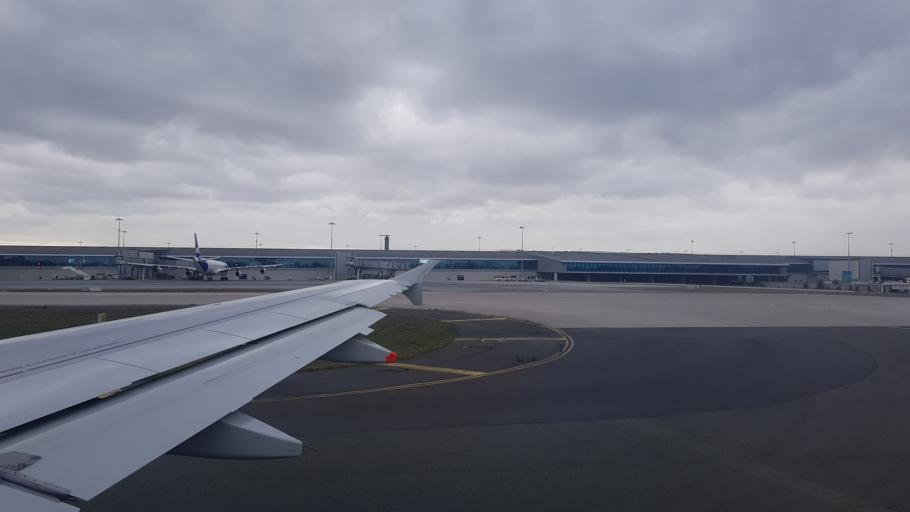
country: FR
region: Ile-de-France
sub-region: Departement de Seine-et-Marne
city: Mitry-Mory
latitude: 49.0039
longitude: 2.5959
